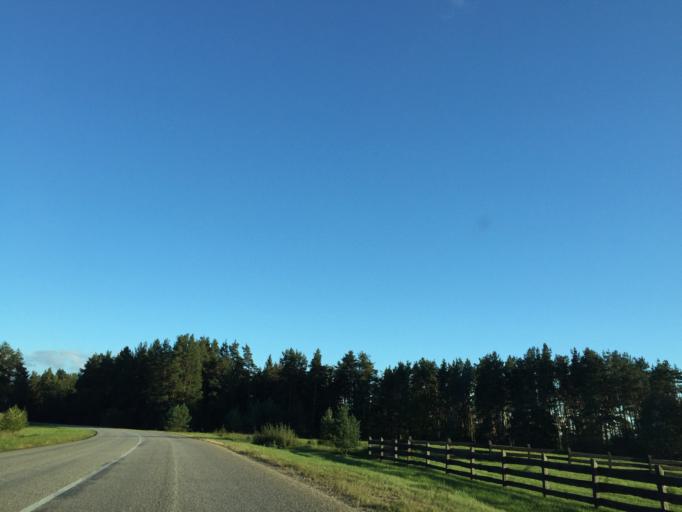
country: LV
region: Kuldigas Rajons
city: Kuldiga
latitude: 56.9141
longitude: 22.0558
